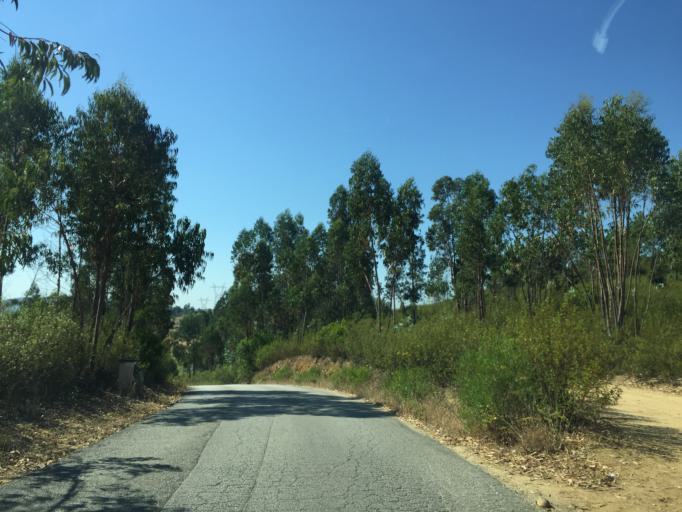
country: PT
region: Santarem
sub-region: Constancia
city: Constancia
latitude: 39.5616
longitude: -8.3214
